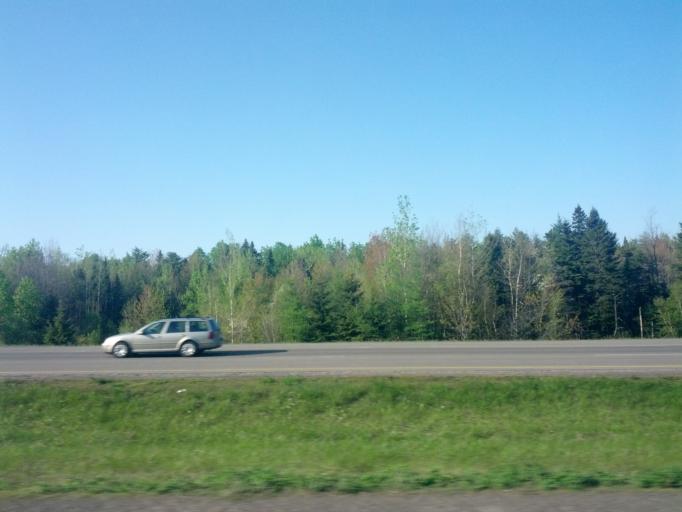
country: CA
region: New Brunswick
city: Moncton
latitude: 46.1160
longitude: -64.8161
